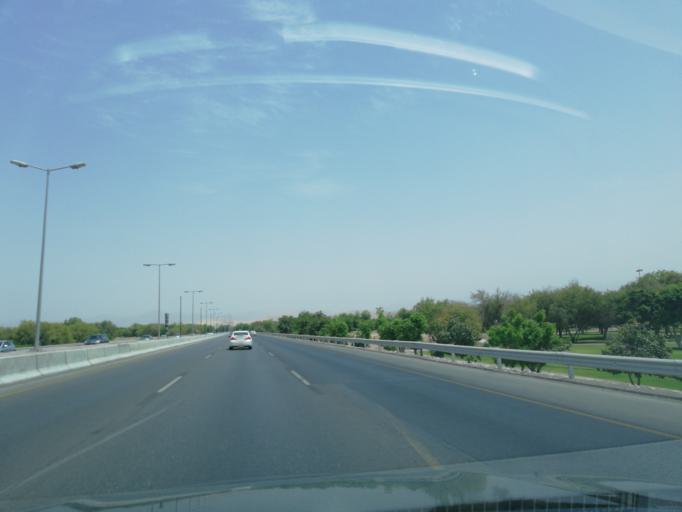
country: OM
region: Muhafazat Masqat
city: As Sib al Jadidah
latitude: 23.5899
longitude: 58.2529
